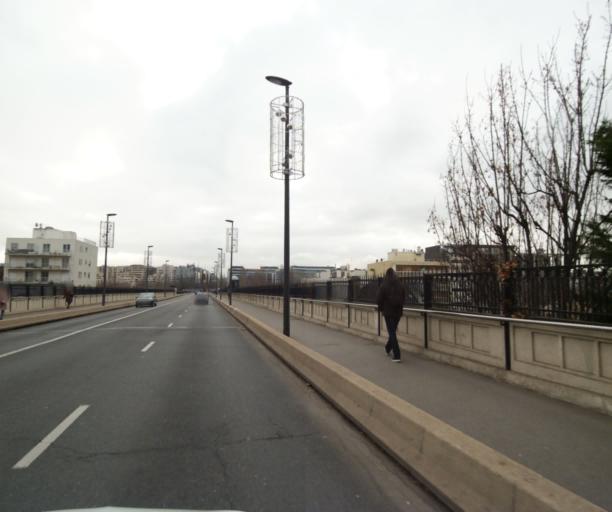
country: FR
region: Ile-de-France
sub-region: Departement des Hauts-de-Seine
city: Levallois-Perret
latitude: 48.9019
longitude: 2.2755
